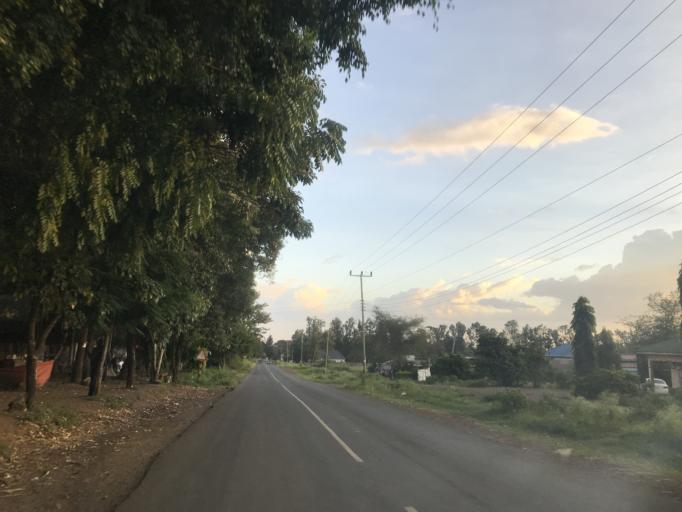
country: TZ
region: Arusha
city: Usa River
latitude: -3.3643
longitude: 36.8688
